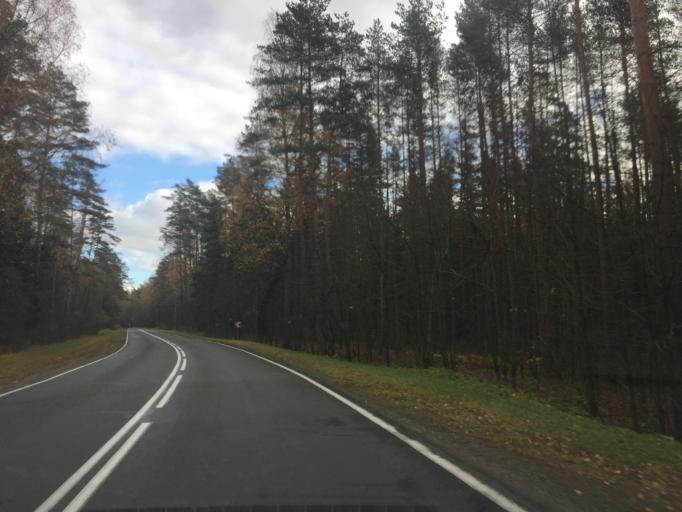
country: BY
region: Minsk
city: Svir
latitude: 54.9217
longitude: 26.5144
